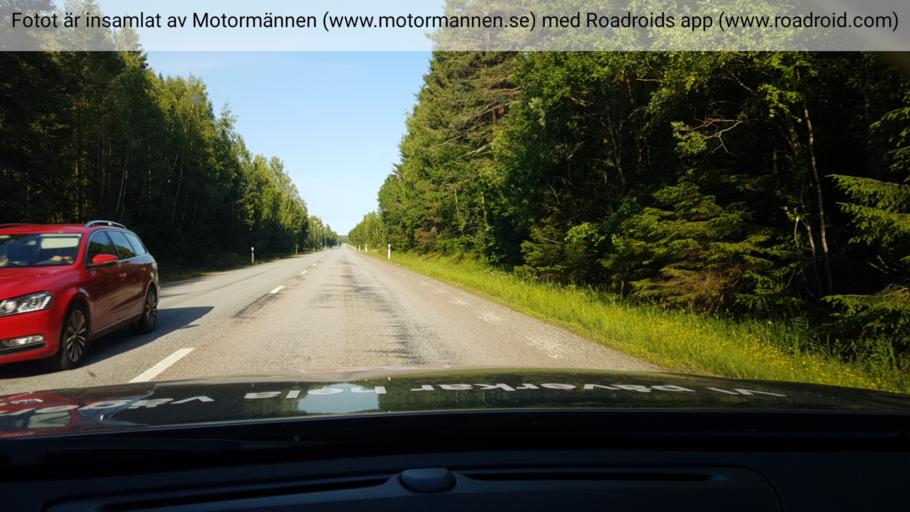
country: SE
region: Uppsala
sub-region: Osthammars Kommun
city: Gimo
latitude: 60.1650
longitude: 18.1519
